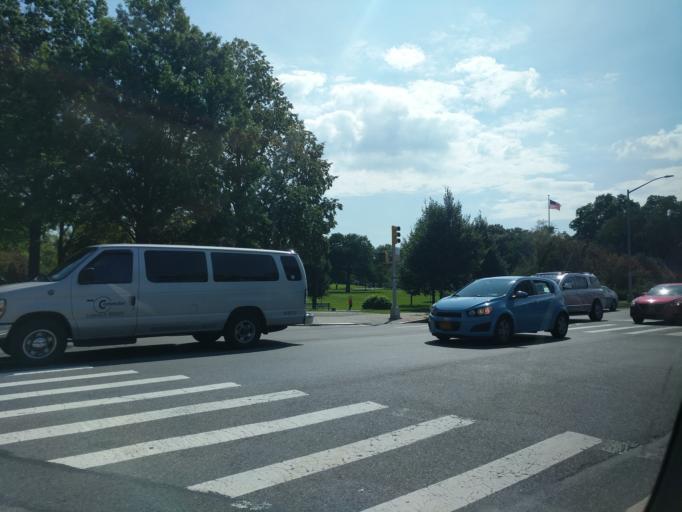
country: US
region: New York
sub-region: Queens County
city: Jamaica
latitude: 40.6931
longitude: -73.7803
